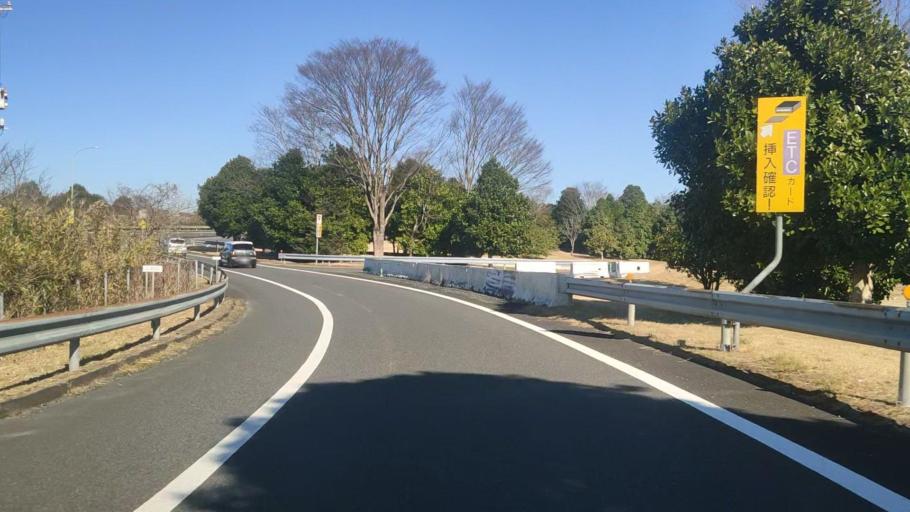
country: JP
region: Miyazaki
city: Miyakonojo
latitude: 31.7810
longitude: 131.1097
